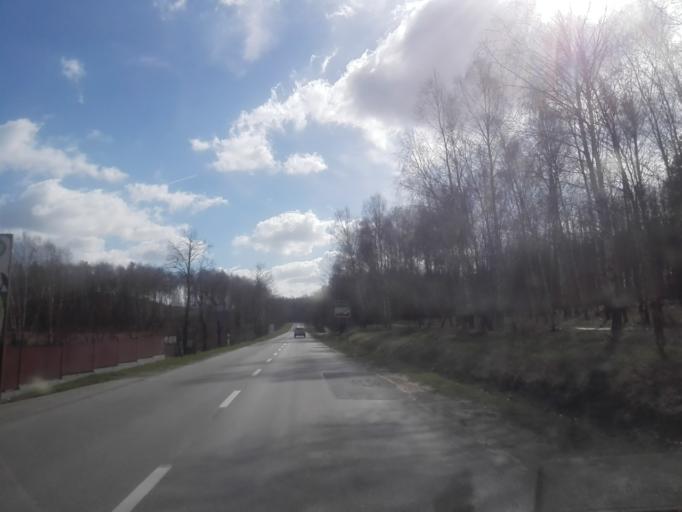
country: PL
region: Silesian Voivodeship
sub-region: Powiat czestochowski
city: Olsztyn
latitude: 50.7524
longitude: 19.2795
